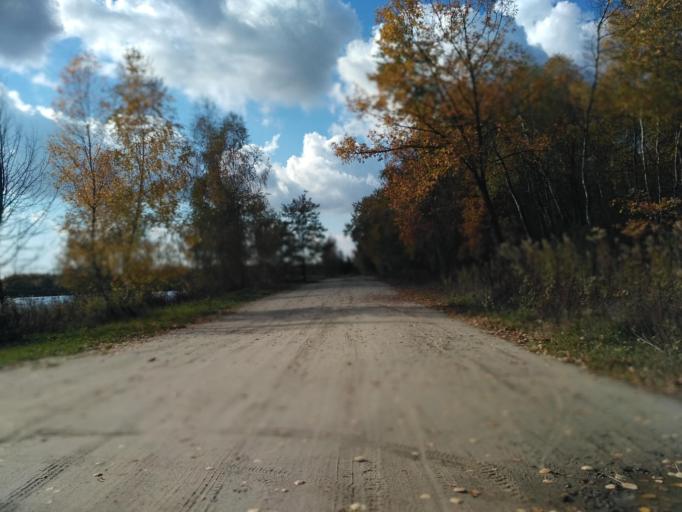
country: PL
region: Subcarpathian Voivodeship
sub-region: Powiat rzeszowski
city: Glogow Malopolski
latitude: 50.1330
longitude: 21.9228
